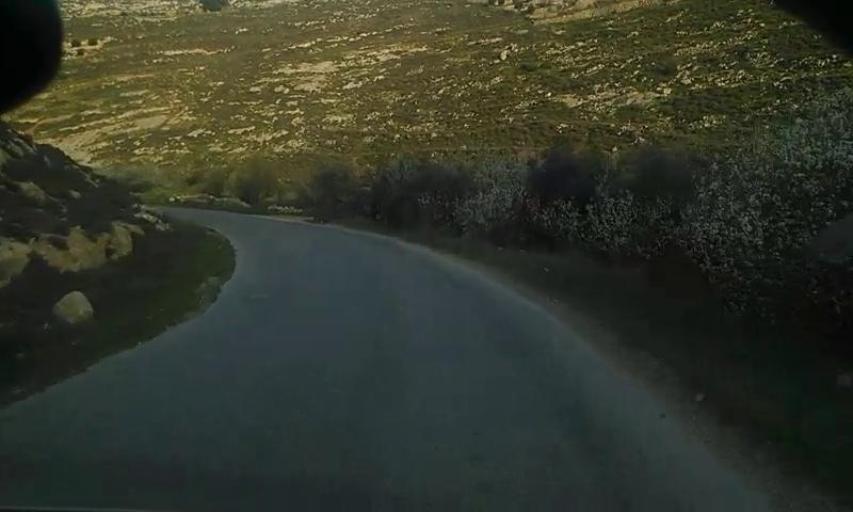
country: PS
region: West Bank
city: Ash Shuyukh
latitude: 31.5962
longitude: 35.1771
